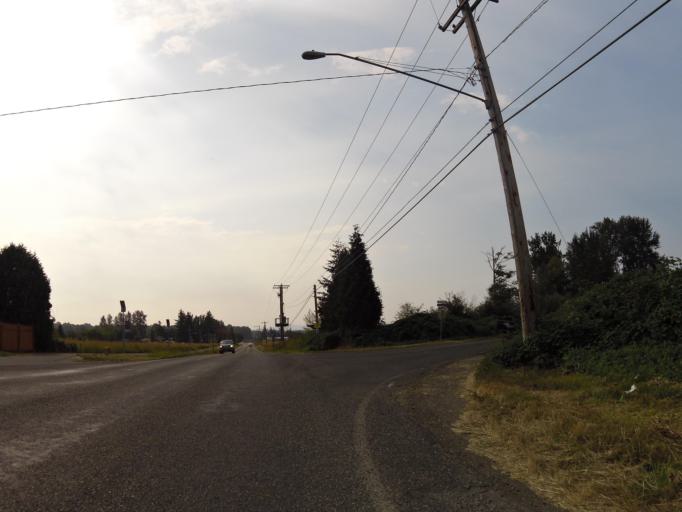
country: US
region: Washington
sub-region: Whatcom County
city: Ferndale
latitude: 48.8097
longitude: -122.6279
